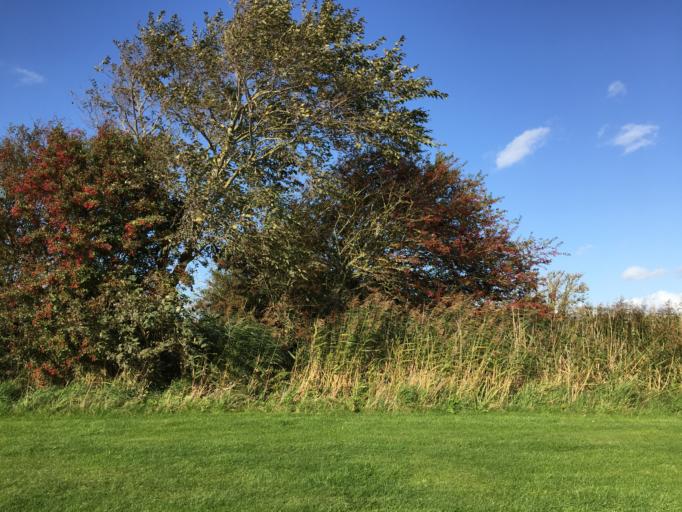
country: DE
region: Schleswig-Holstein
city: Klanxbull
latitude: 54.9560
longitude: 8.6857
